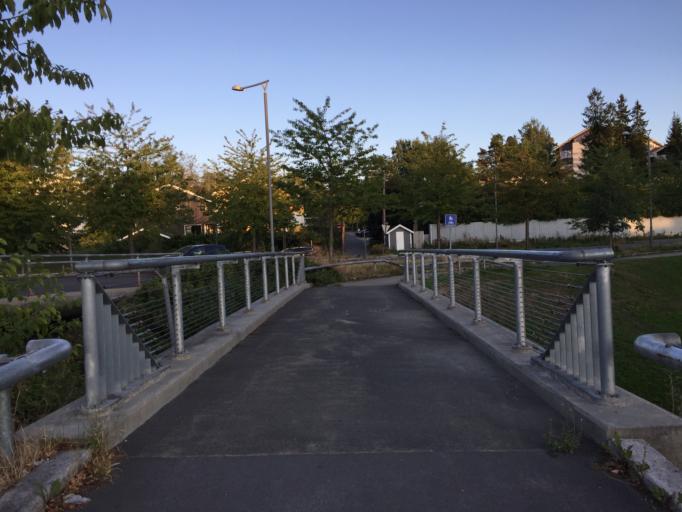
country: NO
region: Akershus
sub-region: Baerum
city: Lysaker
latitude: 59.8901
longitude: 10.6221
